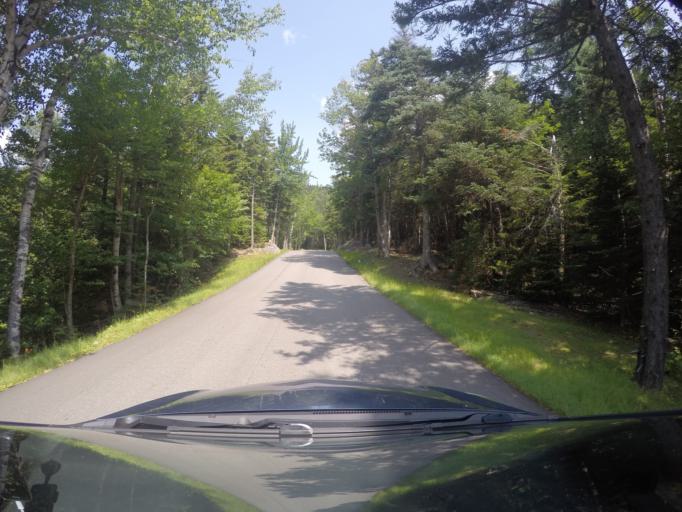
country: US
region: New Hampshire
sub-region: Coos County
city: Gorham
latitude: 44.2801
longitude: -71.2430
